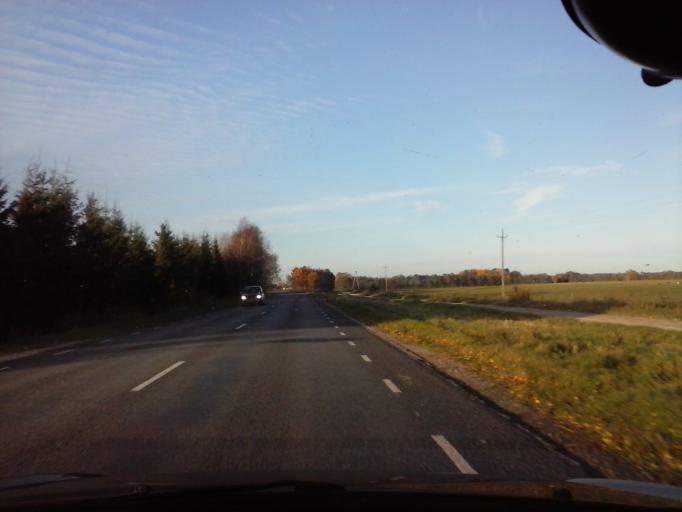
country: EE
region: Laeaene
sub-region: Ridala Parish
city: Uuemoisa
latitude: 58.9593
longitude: 23.7832
